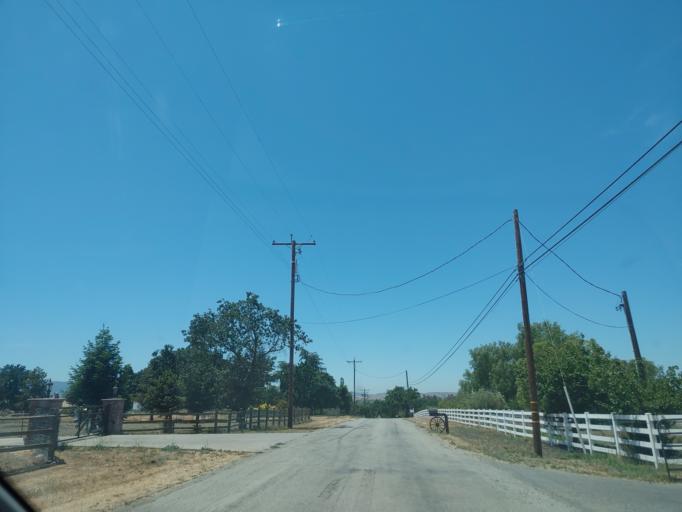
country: US
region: California
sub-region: San Benito County
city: Hollister
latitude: 36.9175
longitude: -121.3490
